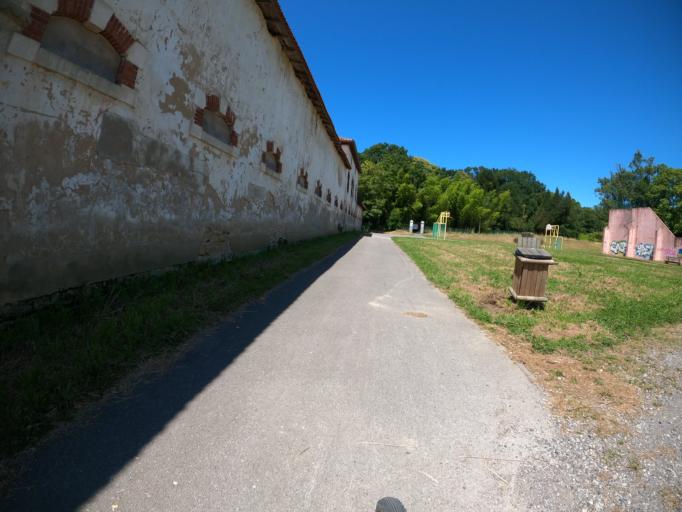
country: FR
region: Aquitaine
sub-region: Departement des Pyrenees-Atlantiques
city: Boucau
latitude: 43.5267
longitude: -1.4545
